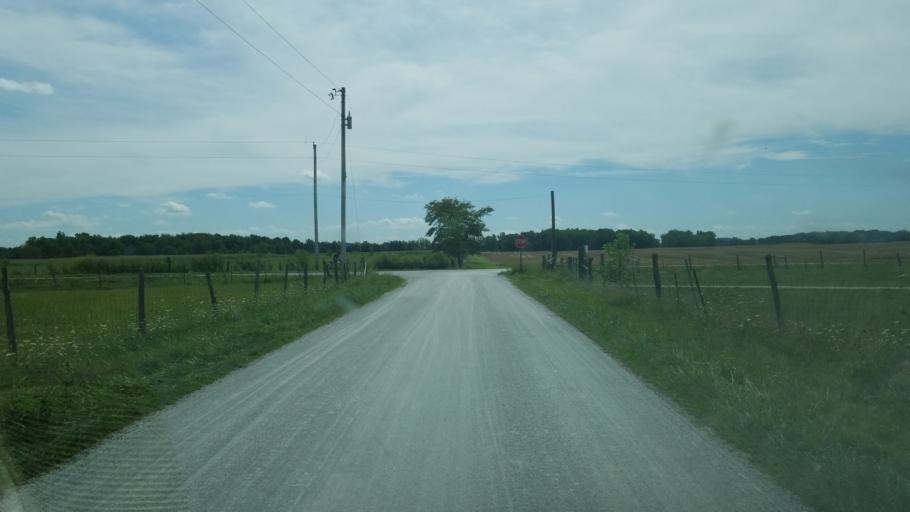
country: US
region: Ohio
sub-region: Hardin County
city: Kenton
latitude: 40.5973
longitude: -83.5544
